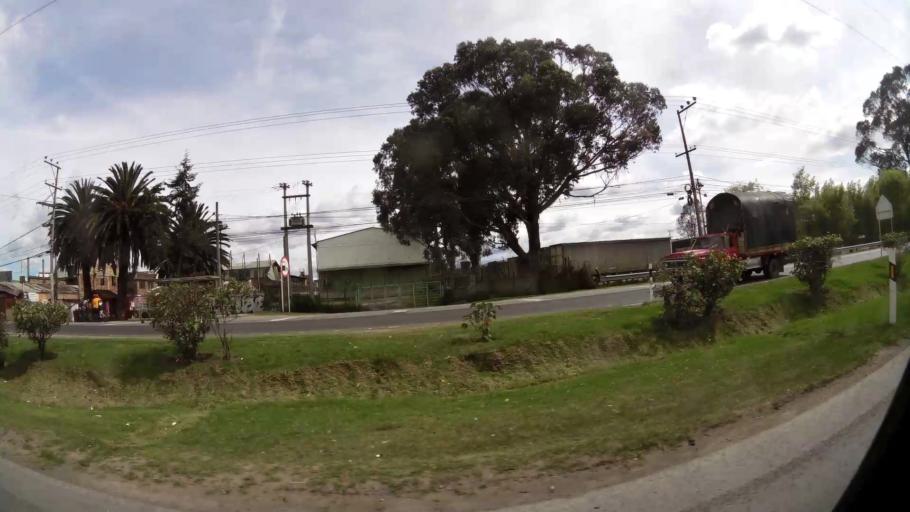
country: CO
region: Cundinamarca
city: Funza
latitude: 4.6992
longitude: -74.1850
